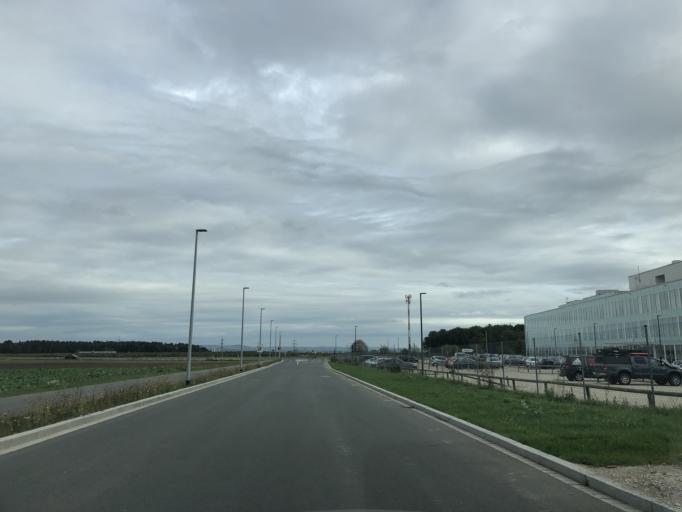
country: DE
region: Bavaria
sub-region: Regierungsbezirk Mittelfranken
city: Herzogenaurach
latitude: 49.5801
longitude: 10.9198
